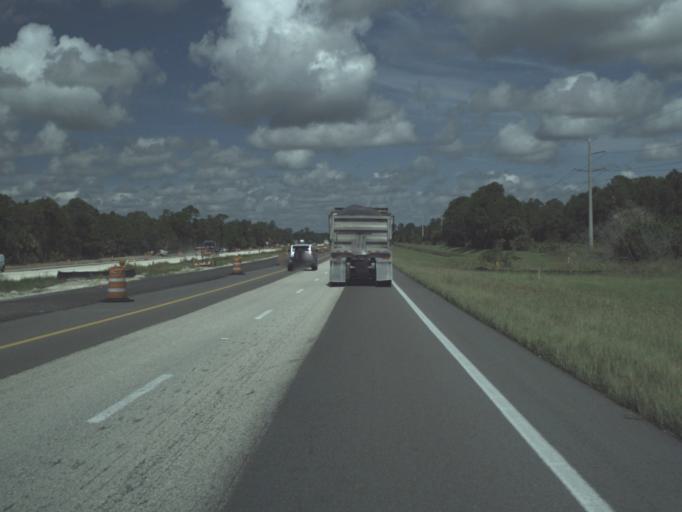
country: US
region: Florida
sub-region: Charlotte County
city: Port Charlotte
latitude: 27.0477
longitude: -82.0711
